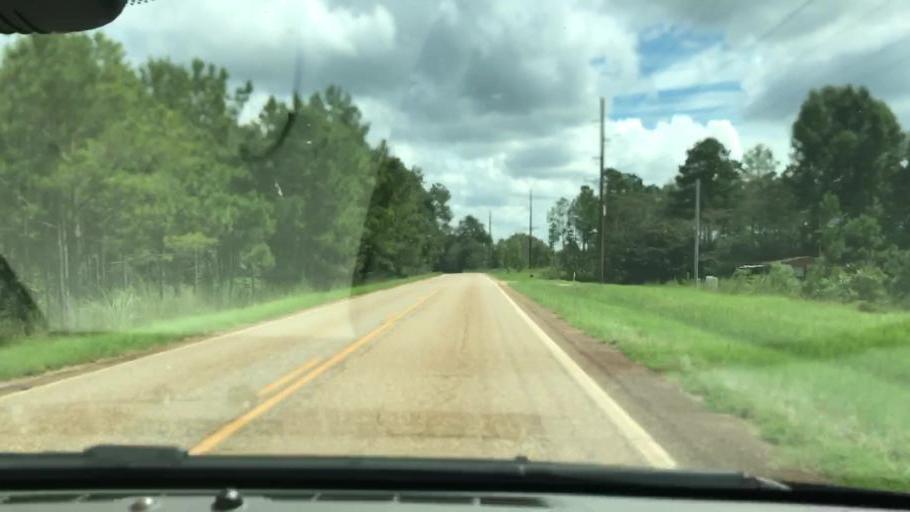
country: US
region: Georgia
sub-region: Stewart County
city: Lumpkin
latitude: 32.0688
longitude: -84.8867
